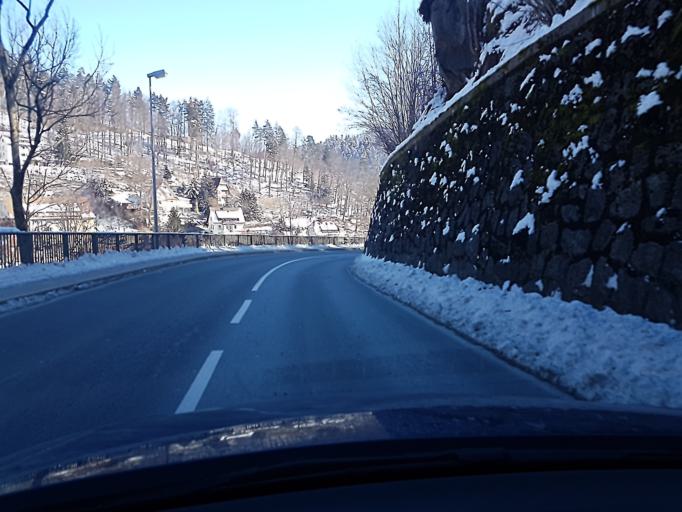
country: DE
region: Baden-Wuerttemberg
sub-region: Freiburg Region
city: Triberg im Schwarzwald
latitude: 48.1320
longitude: 8.2261
